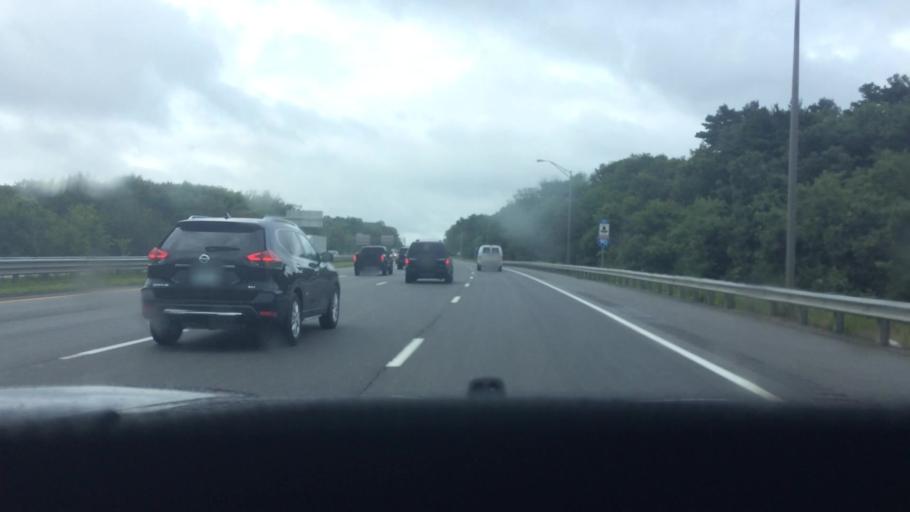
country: US
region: Massachusetts
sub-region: Worcester County
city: Sturbridge
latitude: 42.1299
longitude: -72.0579
